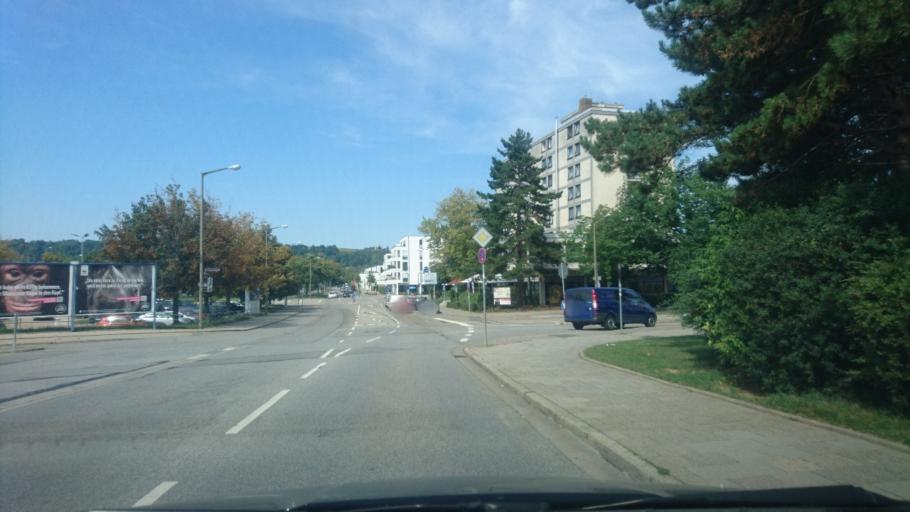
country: DE
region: Bavaria
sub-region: Upper Palatinate
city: Sinzing
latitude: 49.0221
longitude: 12.0568
